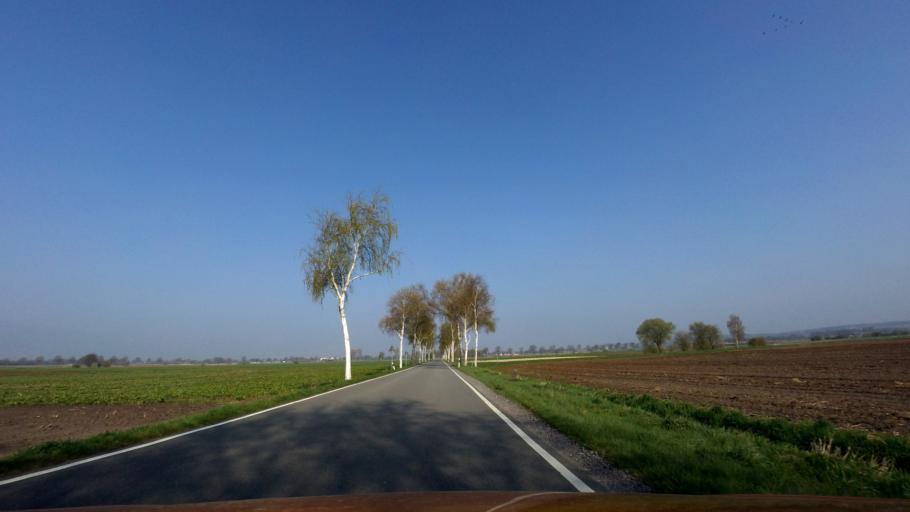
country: DE
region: Lower Saxony
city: Neuenkirchen
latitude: 52.4644
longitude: 8.1173
